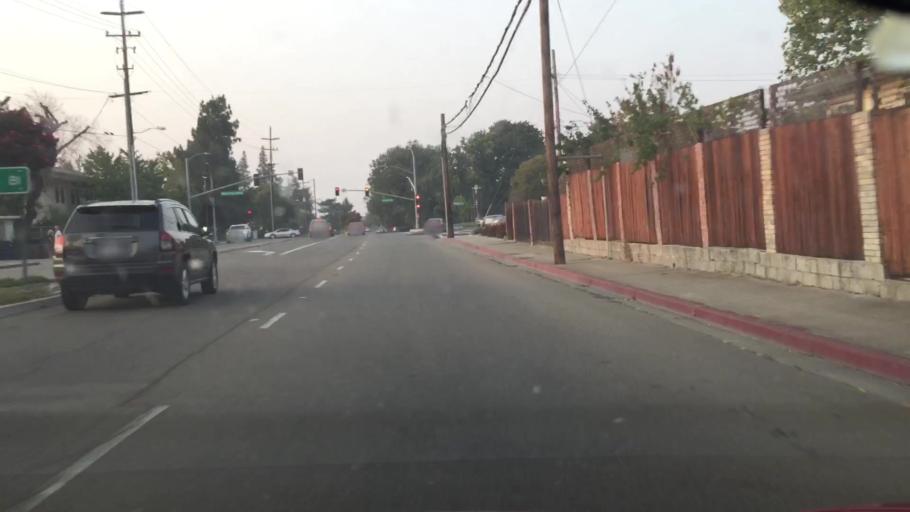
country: US
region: California
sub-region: Alameda County
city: Livermore
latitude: 37.6749
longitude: -121.7799
